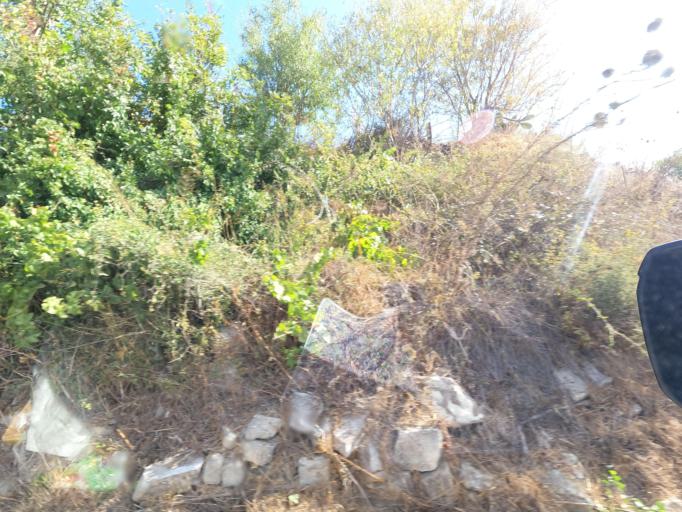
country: CY
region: Pafos
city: Mesogi
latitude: 34.8451
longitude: 32.5264
